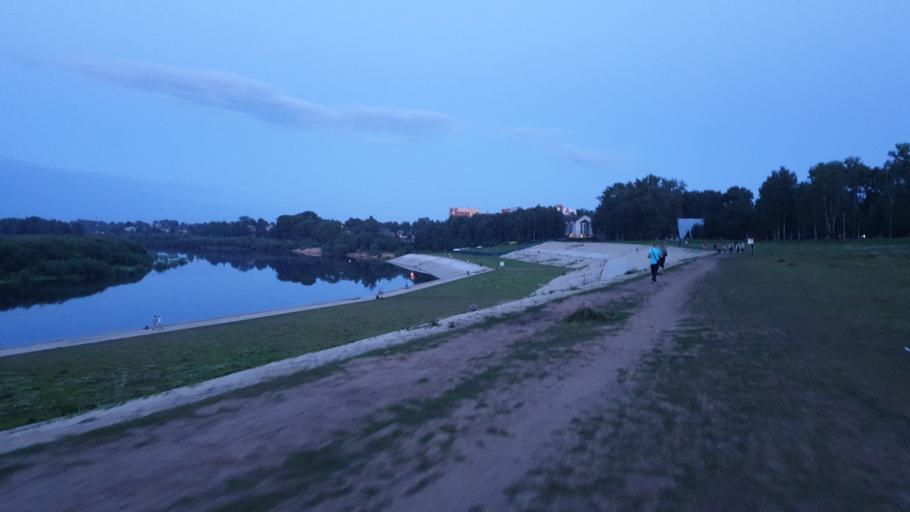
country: RU
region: Komi Republic
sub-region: Syktyvdinskiy Rayon
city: Syktyvkar
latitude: 61.6733
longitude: 50.8435
